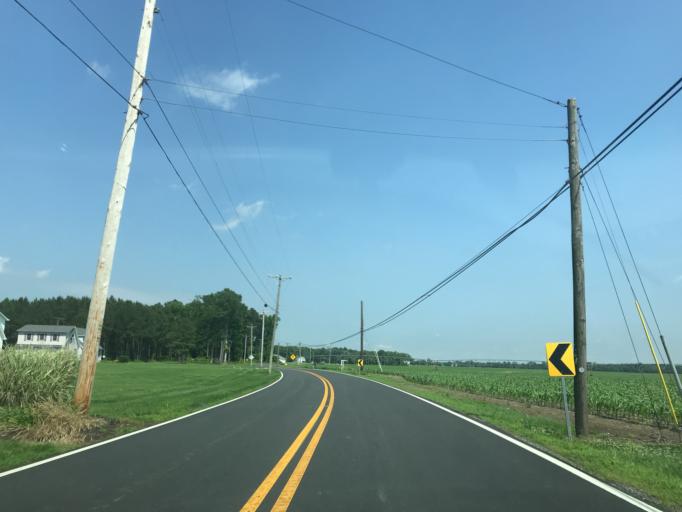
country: US
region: Maryland
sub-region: Dorchester County
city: Hurlock
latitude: 38.5753
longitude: -75.8187
